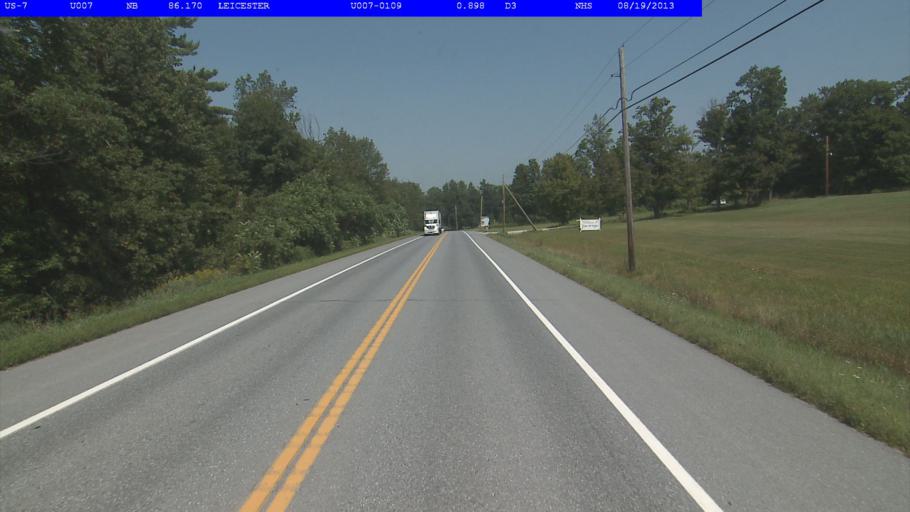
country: US
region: Vermont
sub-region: Rutland County
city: Brandon
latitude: 43.8563
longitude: -73.1063
